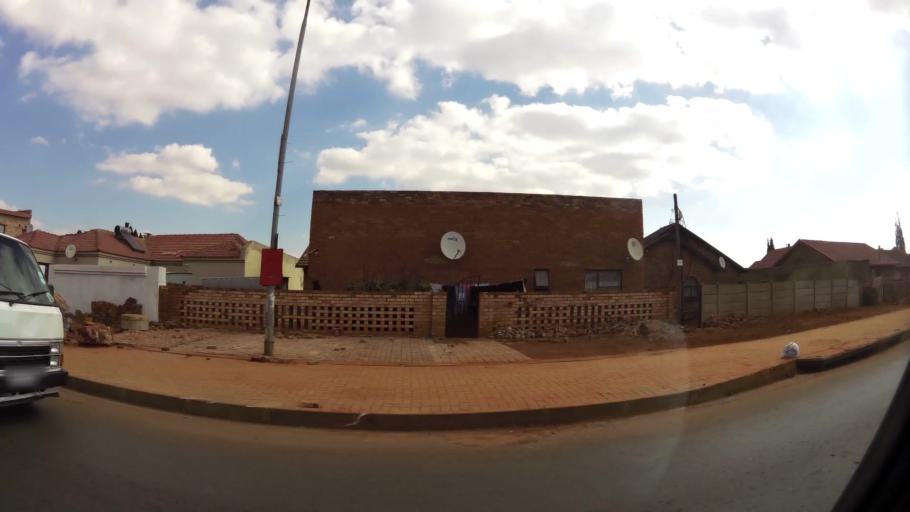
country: ZA
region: Gauteng
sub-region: Ekurhuleni Metropolitan Municipality
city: Tembisa
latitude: -25.9858
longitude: 28.2435
